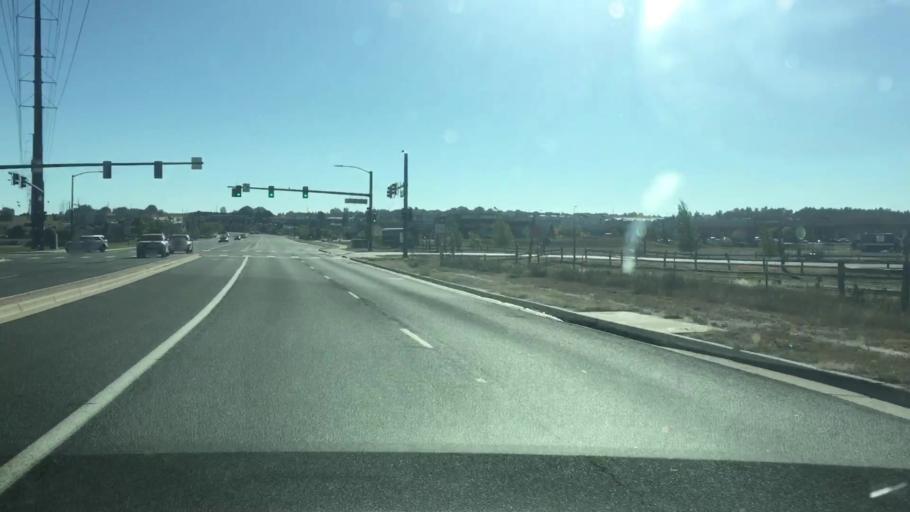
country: US
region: Colorado
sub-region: Douglas County
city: Parker
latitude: 39.5109
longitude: -104.7713
